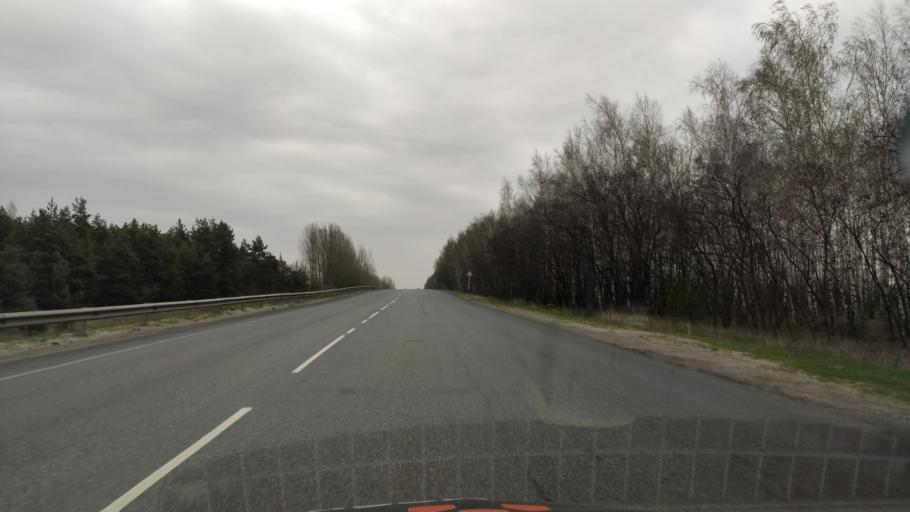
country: RU
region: Kursk
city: Gorshechnoye
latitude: 51.4795
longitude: 37.9548
